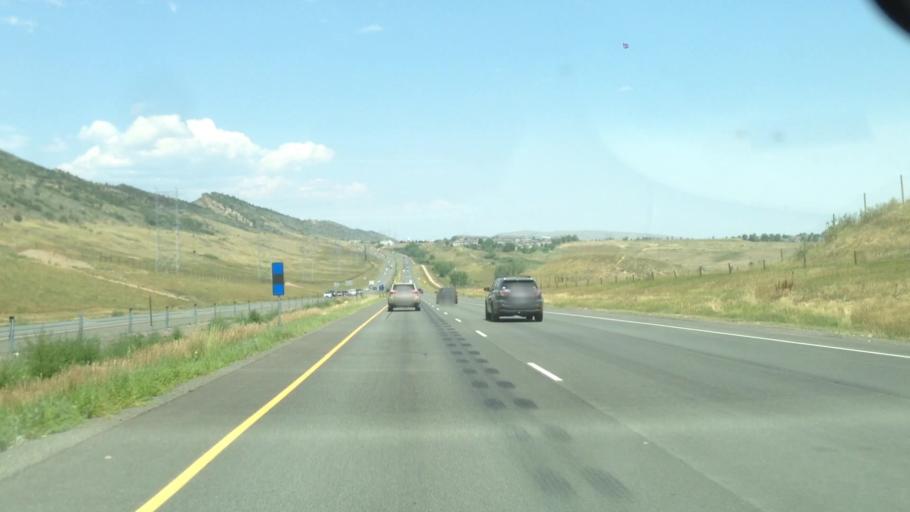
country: US
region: Colorado
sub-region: Jefferson County
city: Ken Caryl
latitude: 39.5833
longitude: -105.1437
